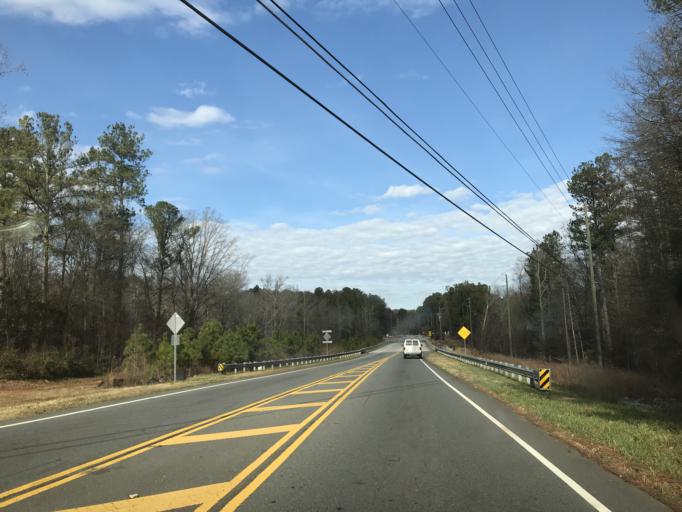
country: US
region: Georgia
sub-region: Douglas County
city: Douglasville
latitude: 33.7945
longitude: -84.8063
